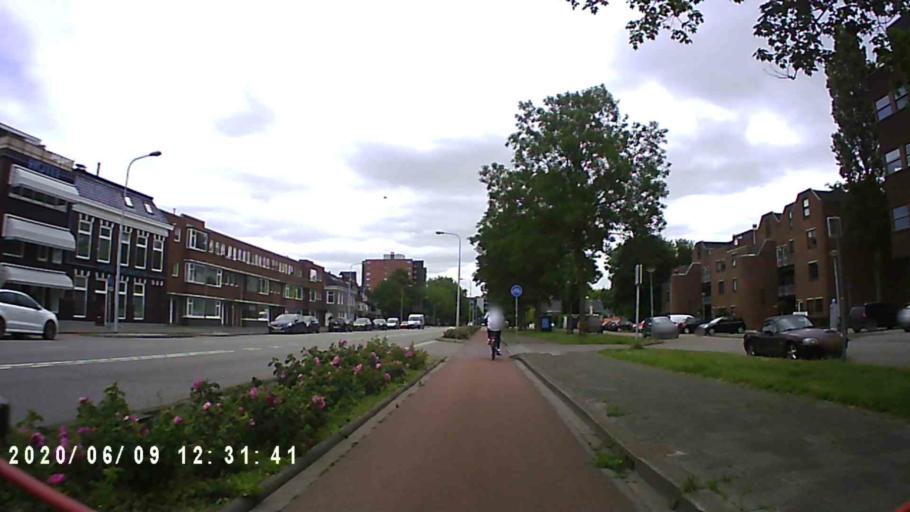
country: NL
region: Groningen
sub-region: Gemeente Groningen
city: Oosterpark
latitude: 53.2190
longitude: 6.5800
